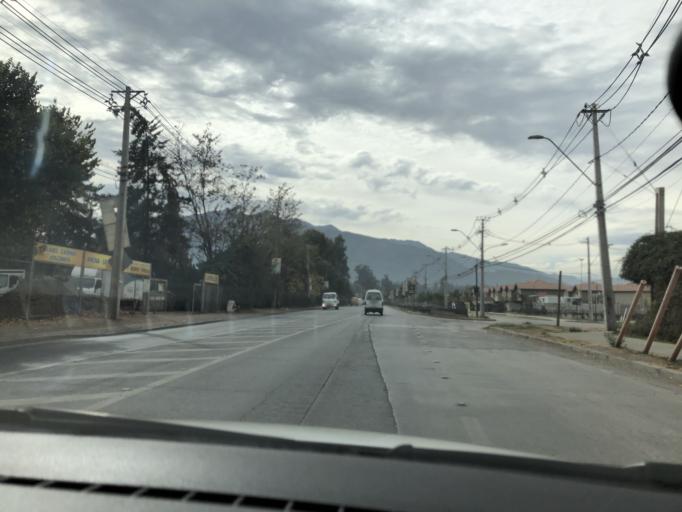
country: CL
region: Santiago Metropolitan
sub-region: Provincia de Cordillera
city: Puente Alto
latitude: -33.6104
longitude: -70.5413
